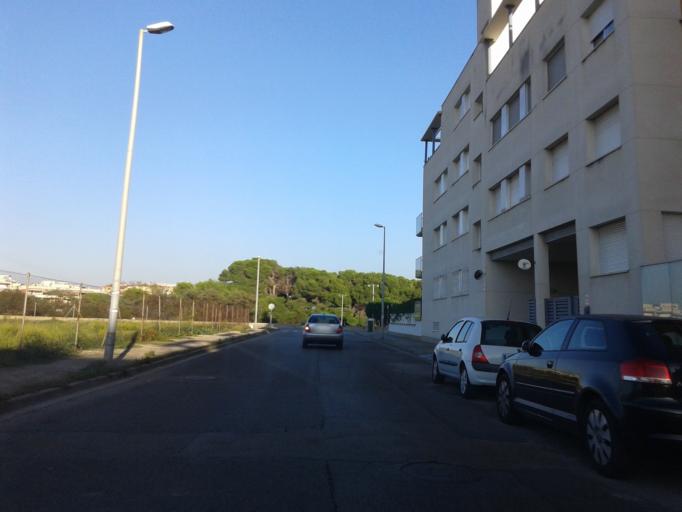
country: ES
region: Catalonia
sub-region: Provincia de Barcelona
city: Cubelles
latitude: 41.1997
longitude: 1.6730
